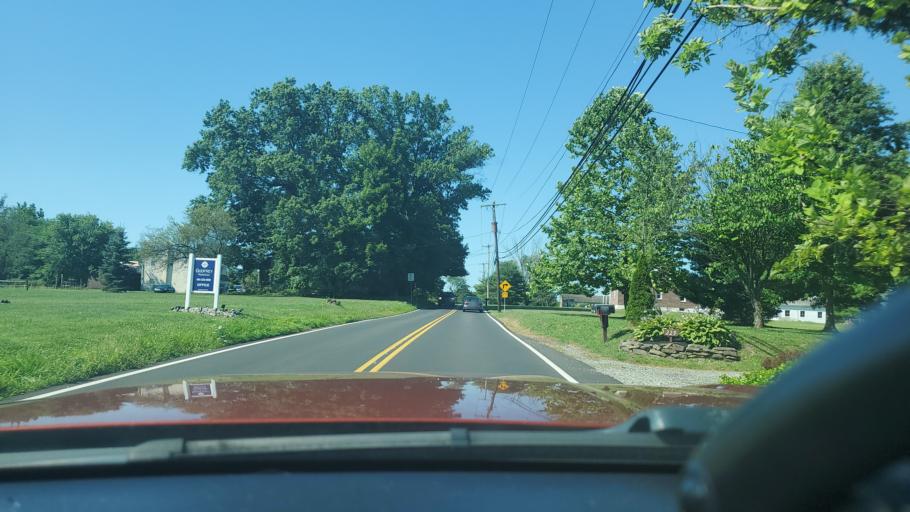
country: US
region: Pennsylvania
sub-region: Montgomery County
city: Limerick
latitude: 40.2496
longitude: -75.5283
